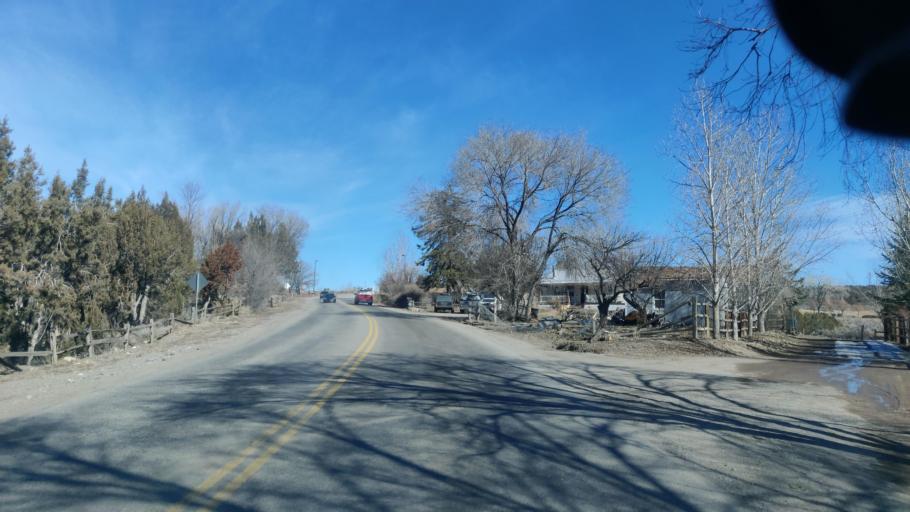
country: US
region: Colorado
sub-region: Garfield County
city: Parachute
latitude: 39.4542
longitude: -108.0362
